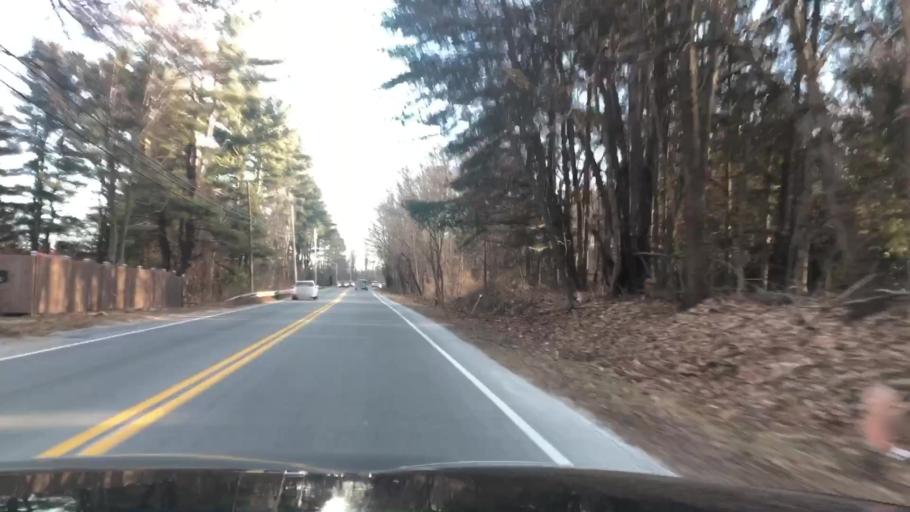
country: US
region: Massachusetts
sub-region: Worcester County
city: Bolton
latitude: 42.4438
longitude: -71.6231
